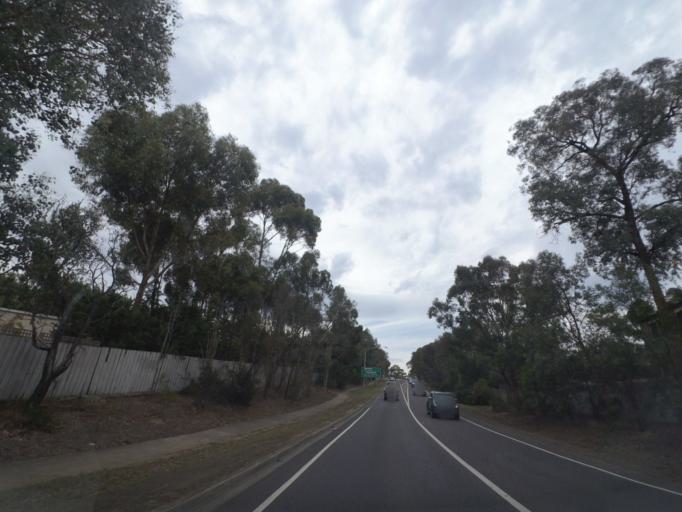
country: AU
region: Victoria
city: Plenty
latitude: -37.6806
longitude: 145.1276
